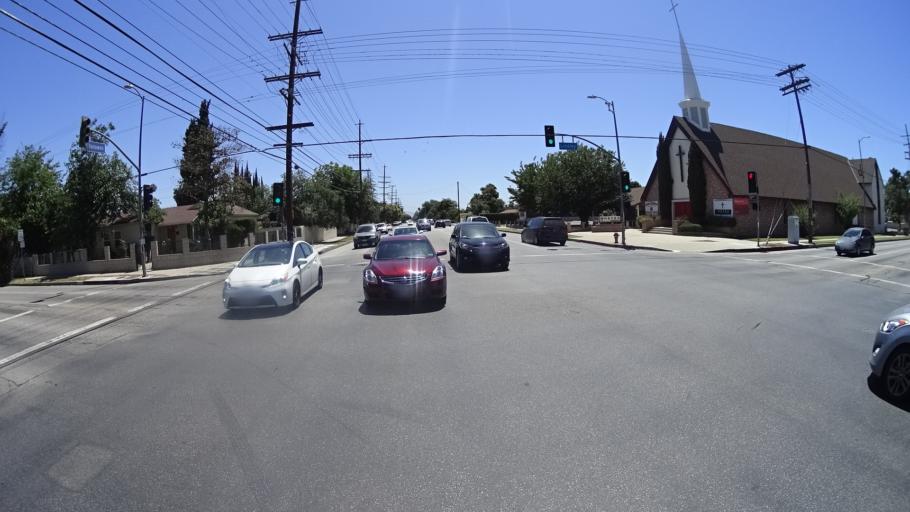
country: US
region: California
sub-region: Los Angeles County
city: Northridge
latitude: 34.1939
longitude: -118.5274
